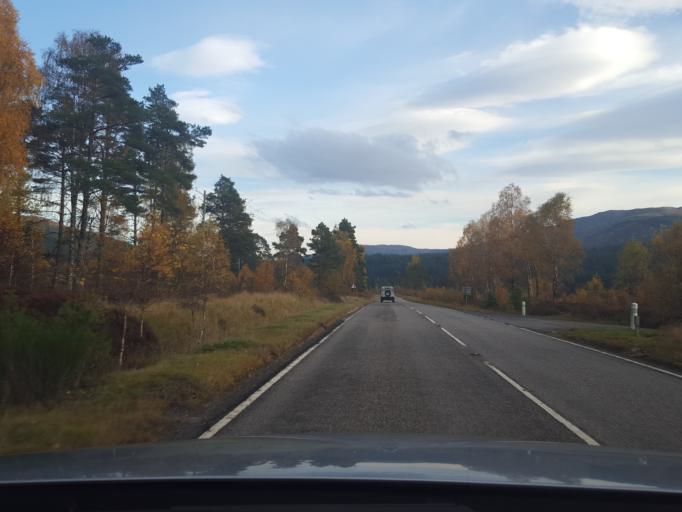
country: GB
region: Scotland
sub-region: Highland
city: Spean Bridge
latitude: 57.1940
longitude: -4.7481
